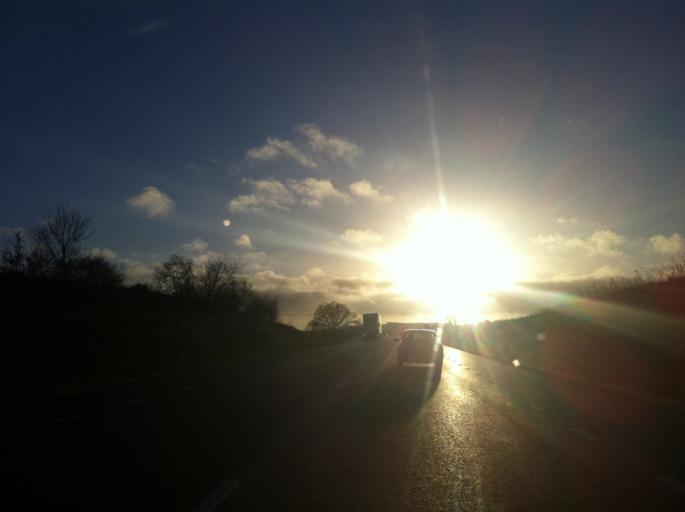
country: SE
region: Skane
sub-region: Hassleholms Kommun
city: Tormestorp
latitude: 56.0751
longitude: 13.7455
